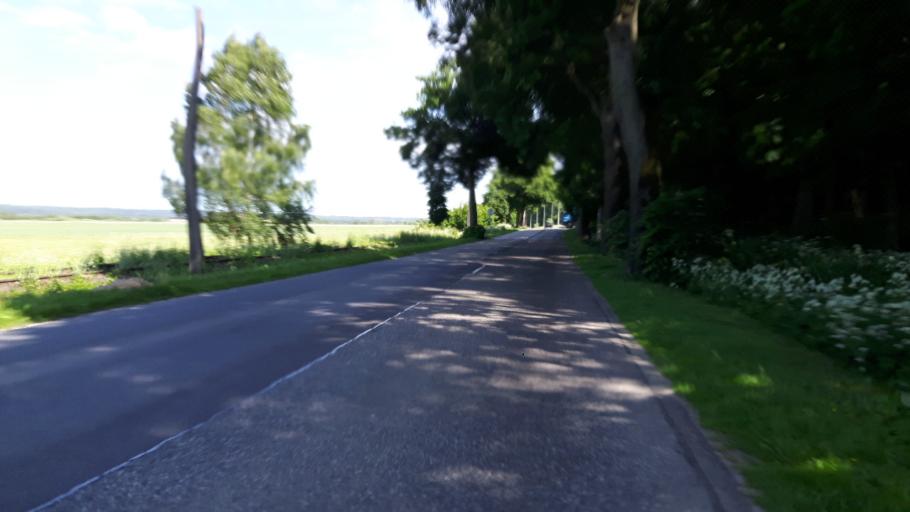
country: PL
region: Pomeranian Voivodeship
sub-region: Powiat wejherowski
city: Orle
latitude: 54.6474
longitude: 18.1101
